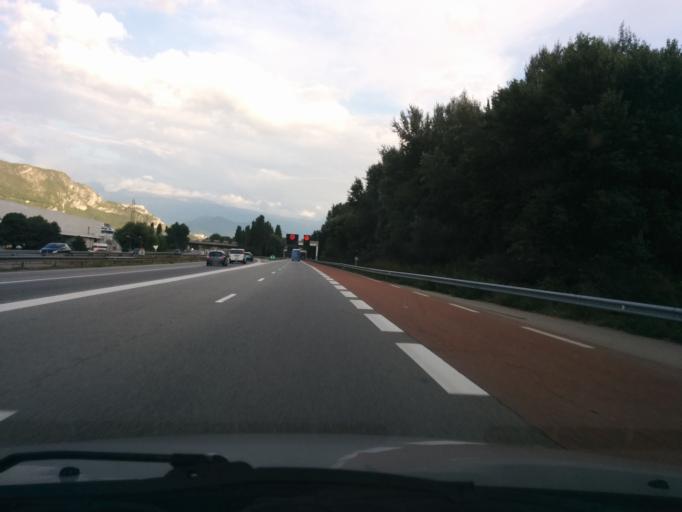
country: FR
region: Rhone-Alpes
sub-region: Departement de l'Isere
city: Sassenage
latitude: 45.2183
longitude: 5.6755
